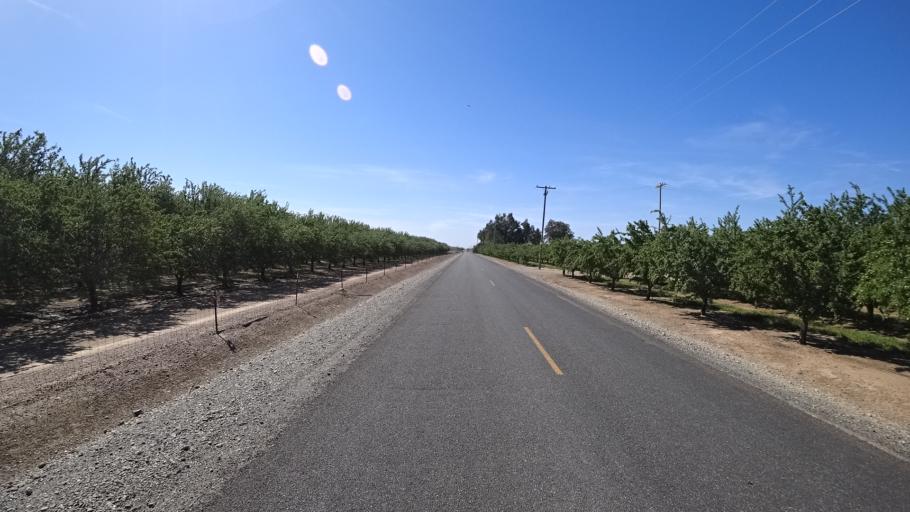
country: US
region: California
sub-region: Glenn County
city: Hamilton City
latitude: 39.6622
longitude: -122.1035
